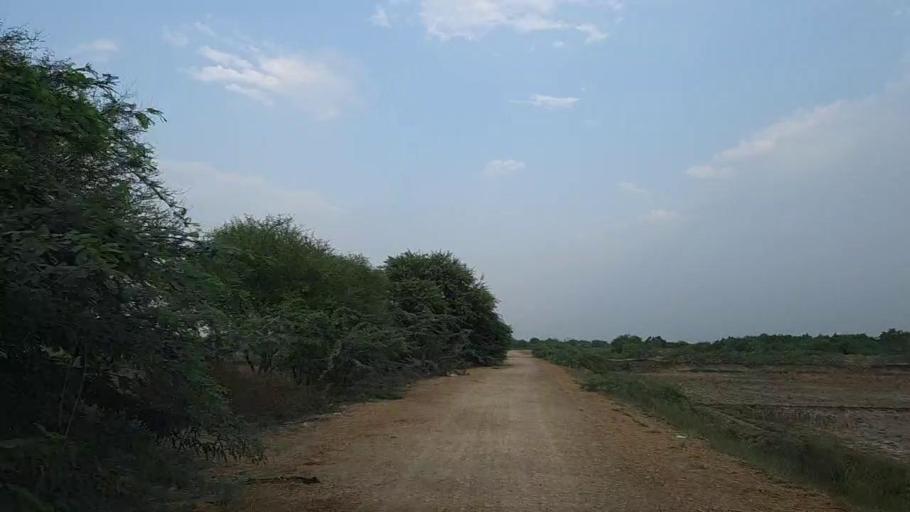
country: PK
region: Sindh
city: Daro Mehar
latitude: 24.7717
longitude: 68.1504
